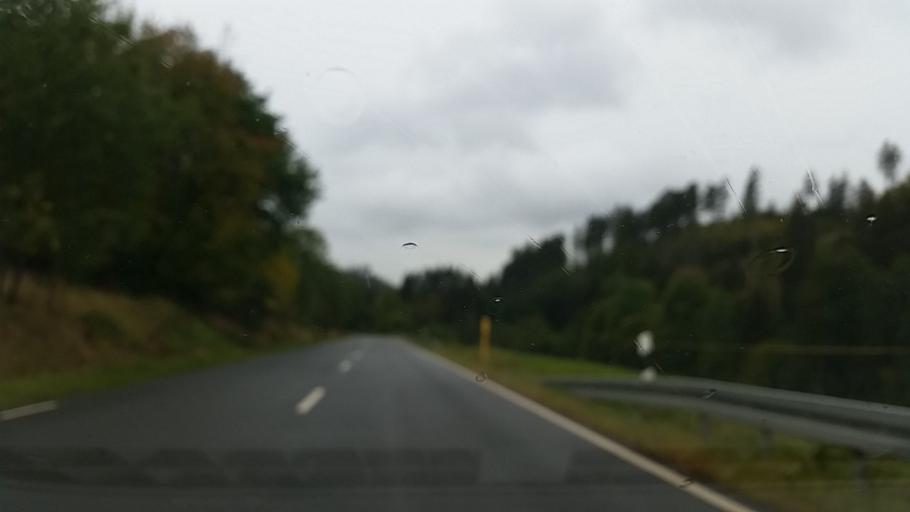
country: DE
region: Lower Saxony
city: Clausthal-Zellerfeld
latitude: 51.7488
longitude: 10.3672
